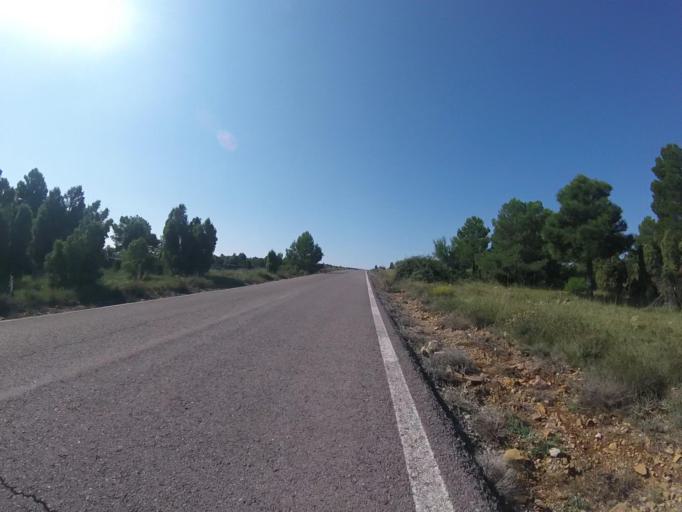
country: ES
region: Valencia
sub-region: Provincia de Castello
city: Benafigos
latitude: 40.2814
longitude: -0.2390
